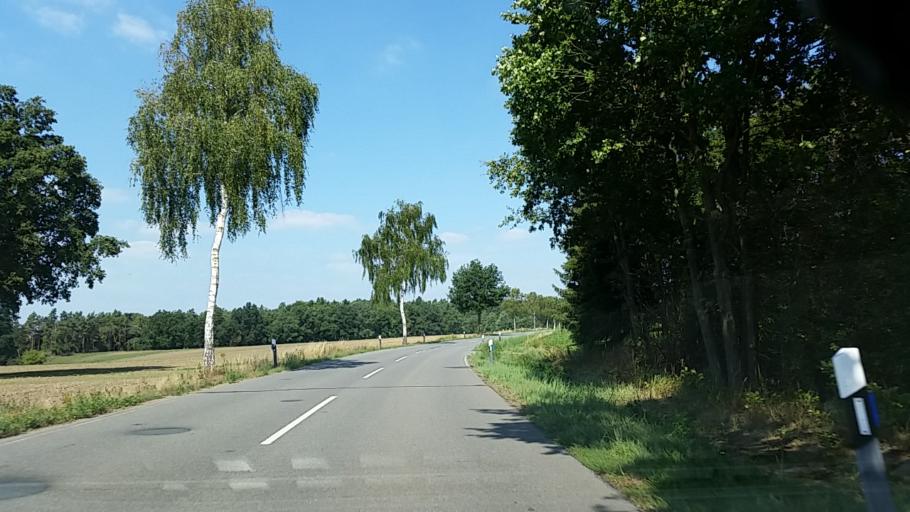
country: DE
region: Lower Saxony
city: Jelmstorf
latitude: 53.1275
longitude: 10.5320
